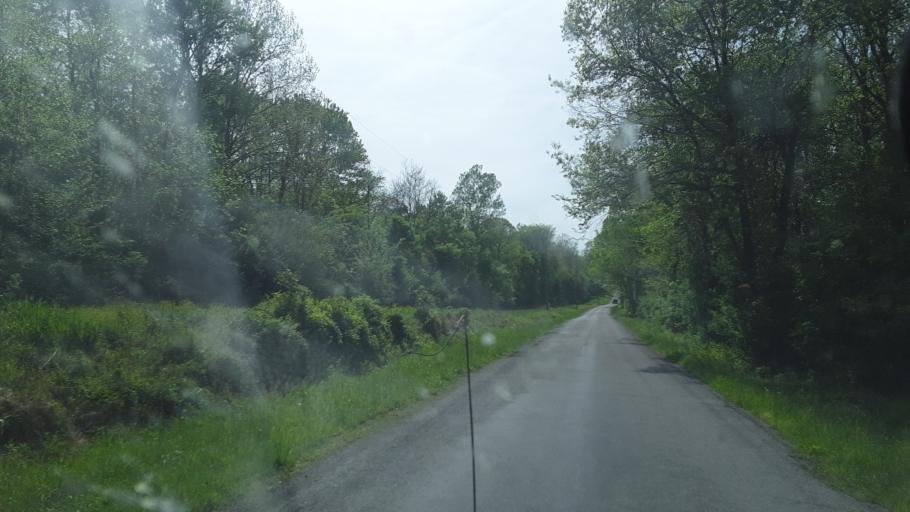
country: US
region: Illinois
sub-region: Jackson County
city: Carbondale
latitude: 37.6798
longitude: -89.2748
